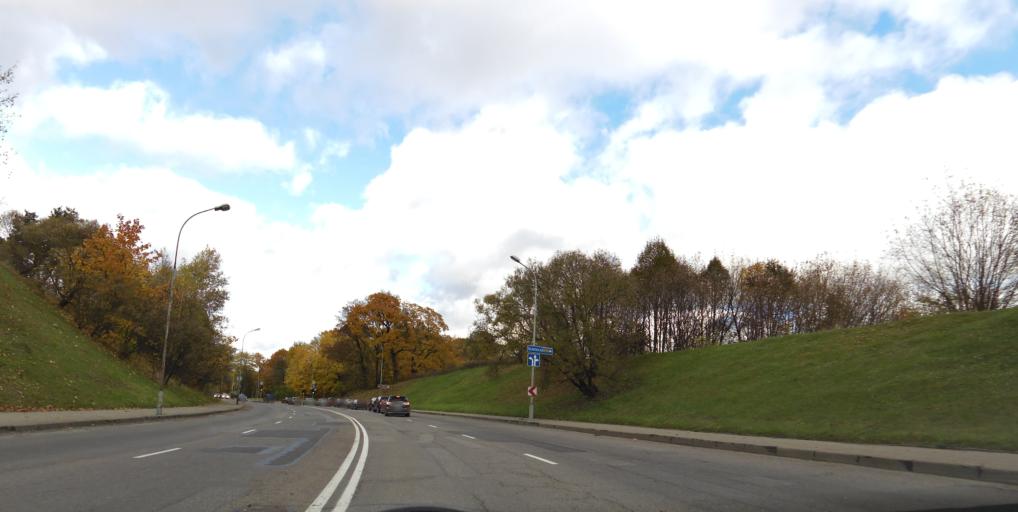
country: LT
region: Vilnius County
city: Rasos
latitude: 54.6653
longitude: 25.3052
